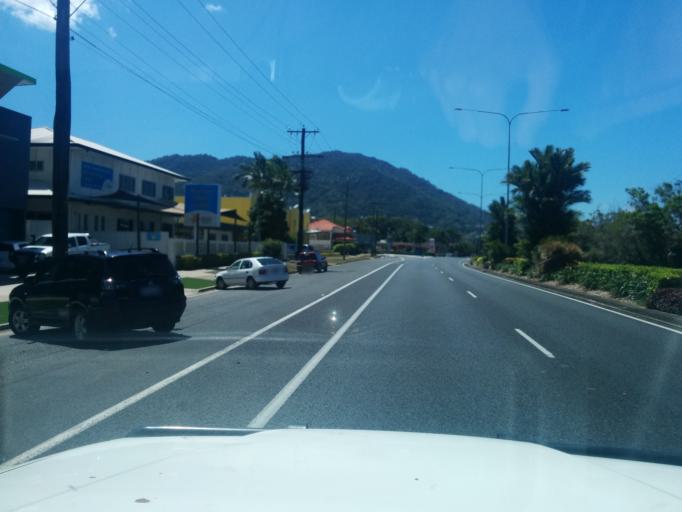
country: AU
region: Queensland
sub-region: Cairns
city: Woree
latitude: -16.9488
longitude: 145.7408
